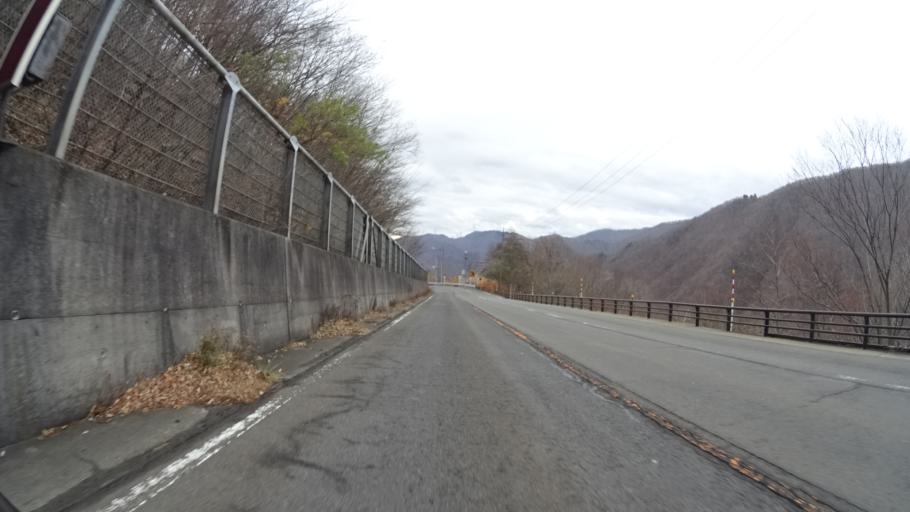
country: JP
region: Gunma
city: Nakanojomachi
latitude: 36.7540
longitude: 138.8331
